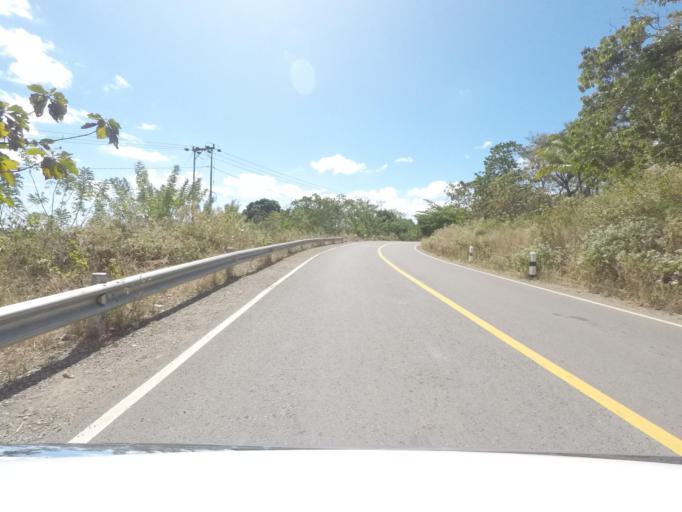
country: TL
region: Baucau
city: Baucau
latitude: -8.4911
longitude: 126.3646
